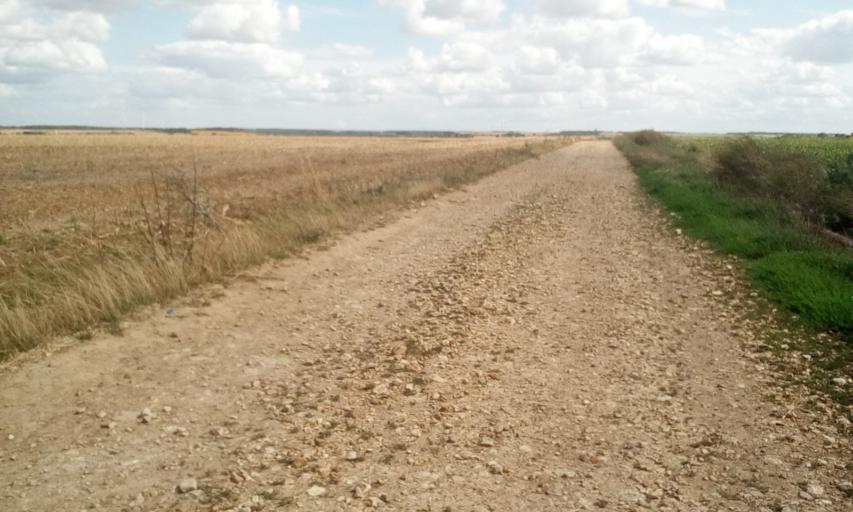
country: FR
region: Lower Normandy
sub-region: Departement du Calvados
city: Bellengreville
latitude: 49.0963
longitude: -0.2259
